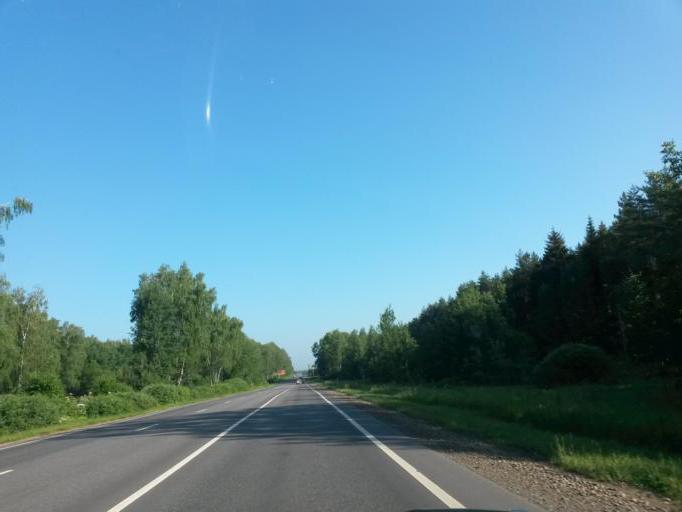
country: RU
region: Moskovskaya
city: Barybino
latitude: 55.2374
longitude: 37.8598
